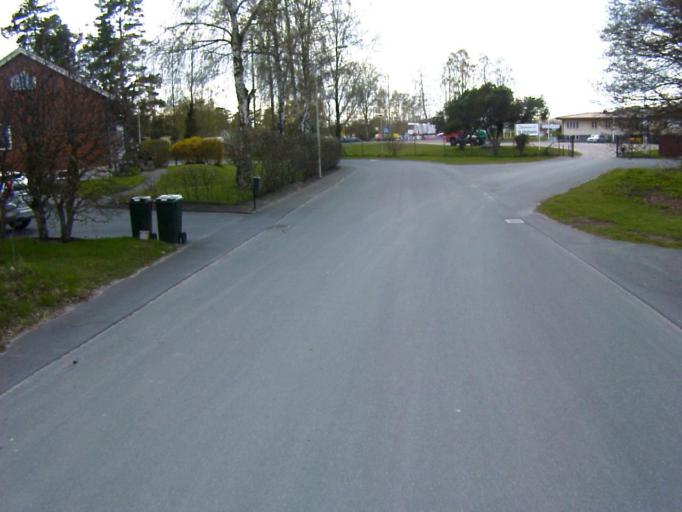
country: SE
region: Skane
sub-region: Kristianstads Kommun
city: Norra Asum
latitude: 56.0016
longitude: 14.0856
